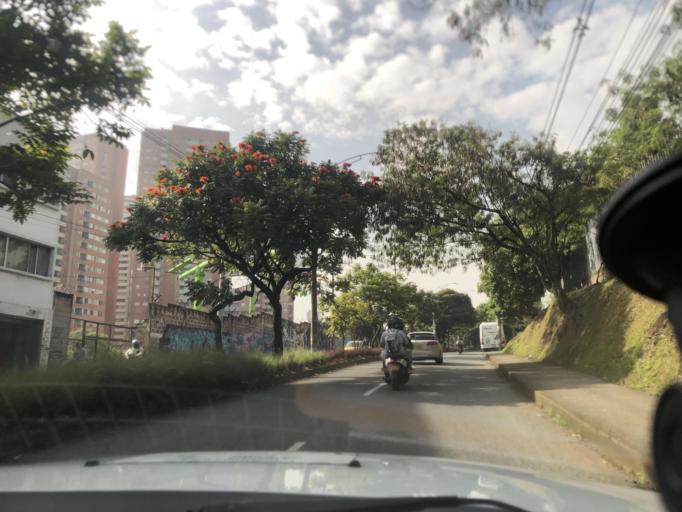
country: CO
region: Antioquia
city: Bello
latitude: 6.3269
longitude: -75.5609
